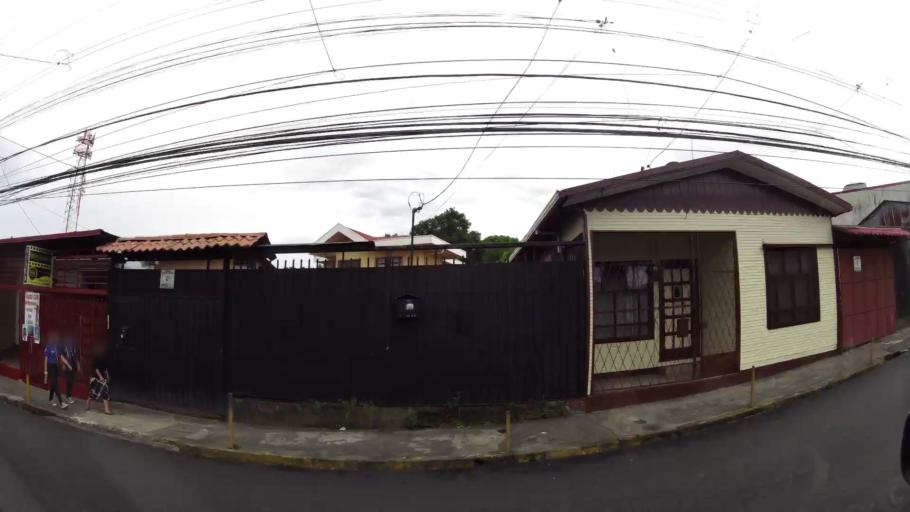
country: CR
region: San Jose
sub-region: Canton de Goicoechea
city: Guadalupe
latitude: 9.9480
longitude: -84.0544
